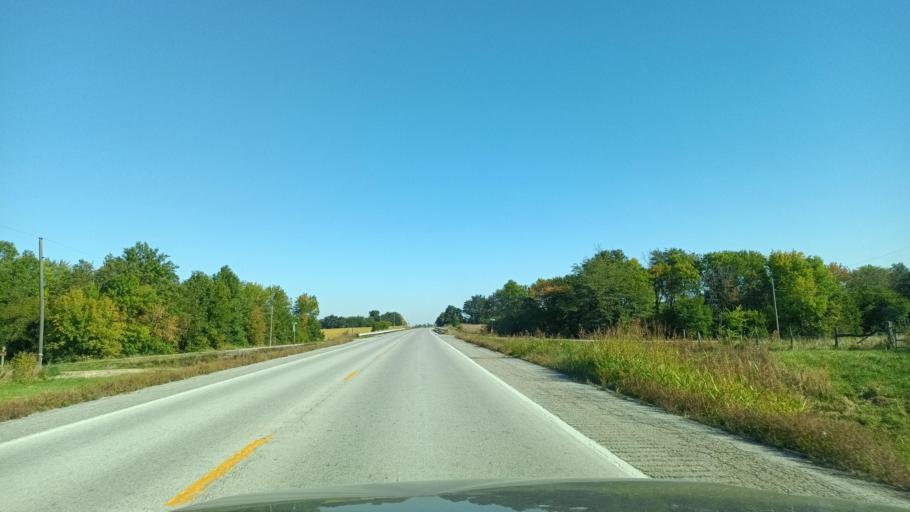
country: US
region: Missouri
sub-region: Audrain County
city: Vandalia
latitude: 39.3094
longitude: -91.6436
